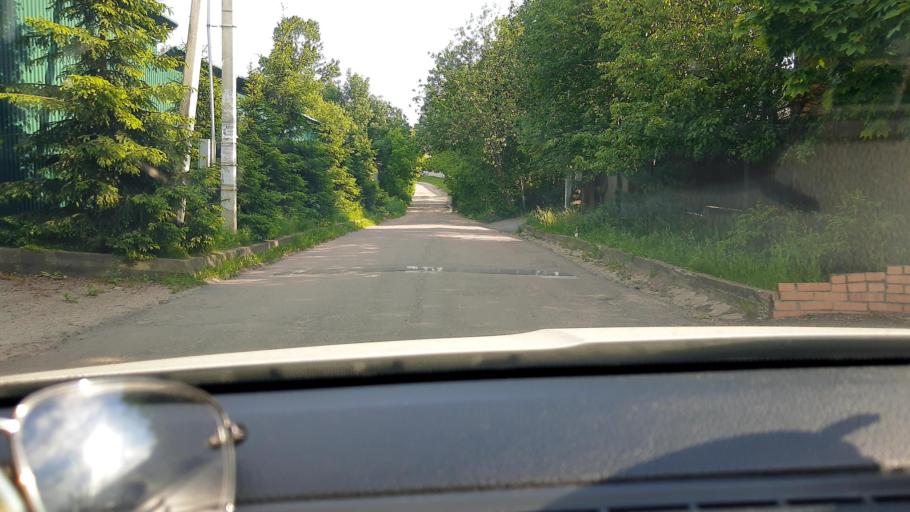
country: RU
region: Moscow
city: Novo-Peredelkino
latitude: 55.6718
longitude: 37.3197
